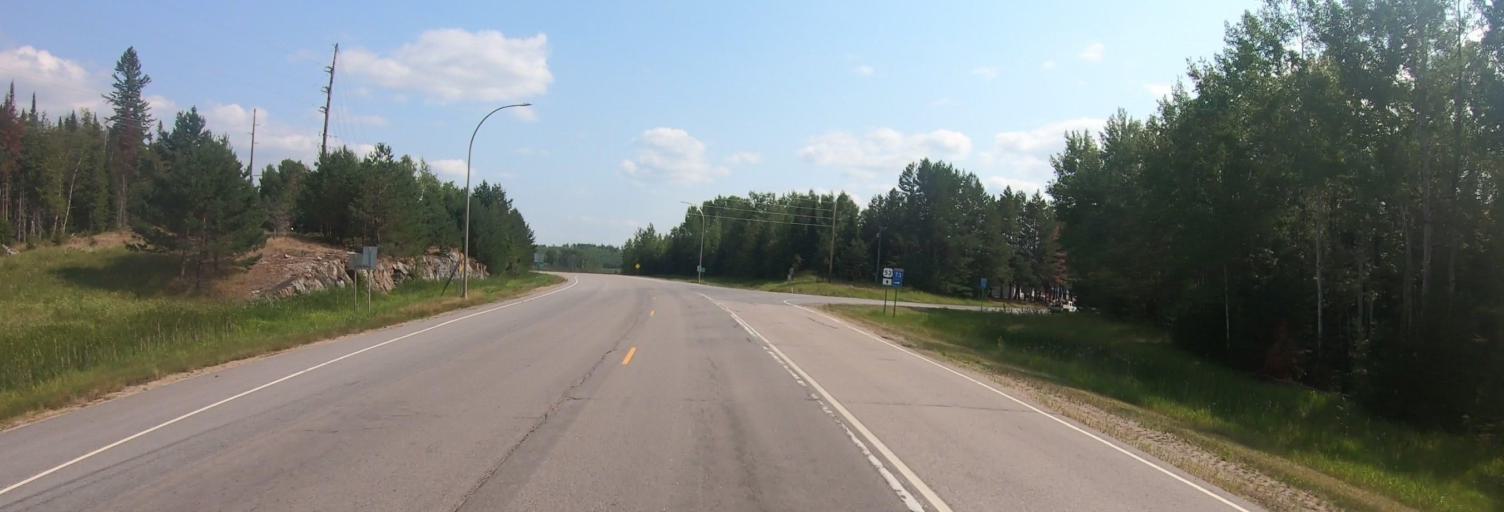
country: US
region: Minnesota
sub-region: Saint Louis County
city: Chisholm
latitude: 47.9287
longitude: -92.8281
